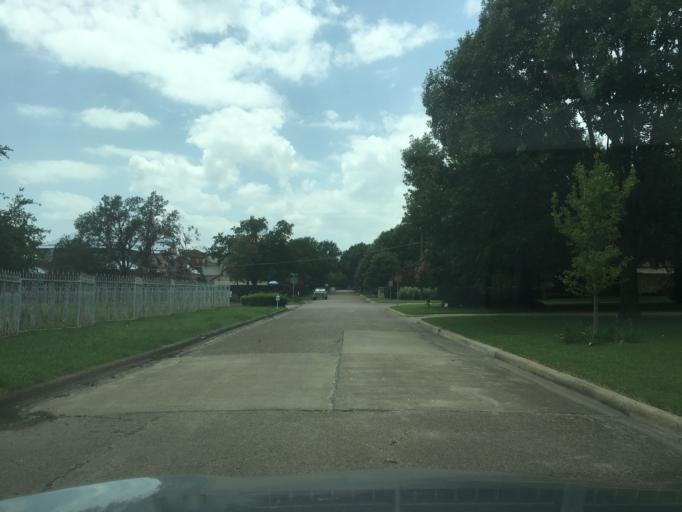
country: US
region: Texas
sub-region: Dallas County
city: University Park
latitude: 32.8915
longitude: -96.8283
